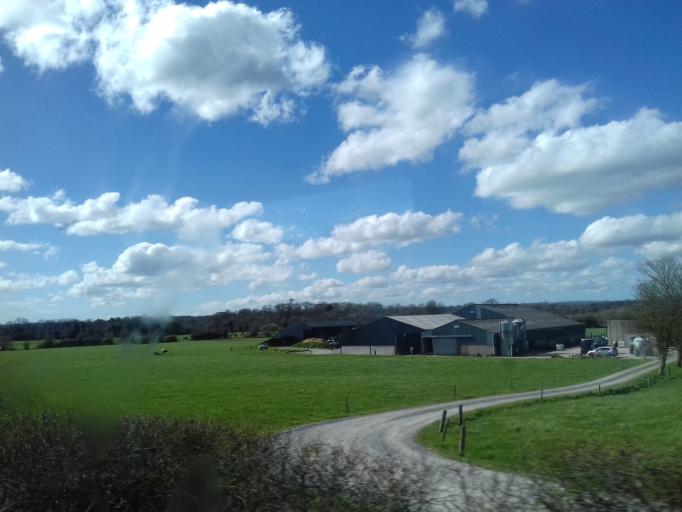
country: IE
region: Munster
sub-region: County Cork
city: Kanturk
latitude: 52.0992
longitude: -8.9644
